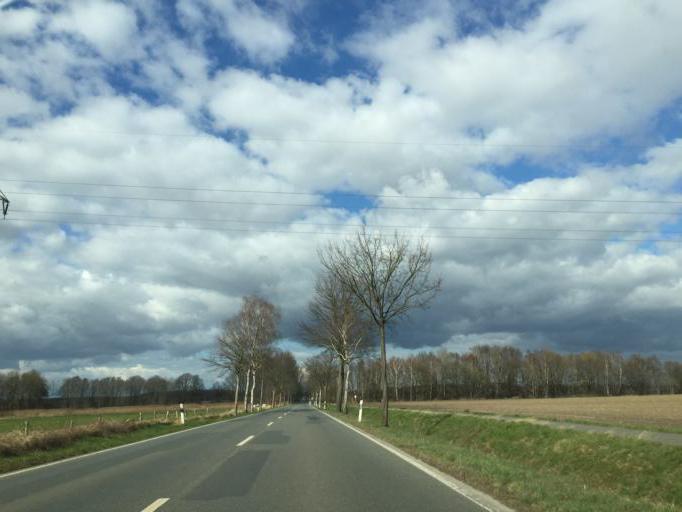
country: DE
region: Lower Saxony
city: Edemissen
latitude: 52.3684
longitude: 10.2491
